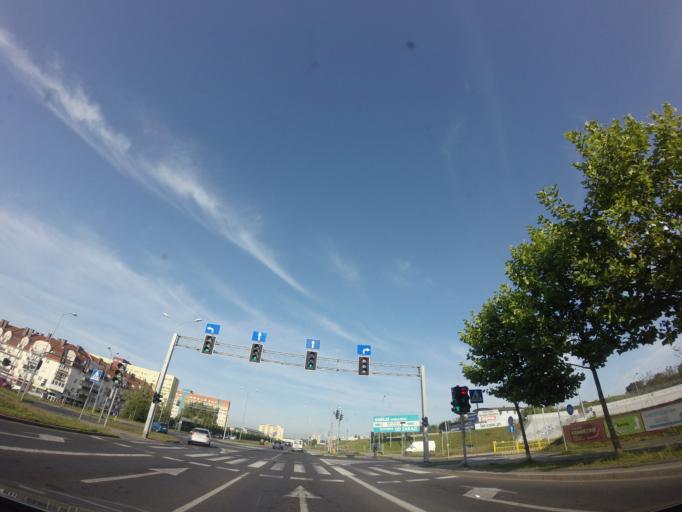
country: PL
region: West Pomeranian Voivodeship
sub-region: Szczecin
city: Szczecin
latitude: 53.4546
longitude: 14.5512
